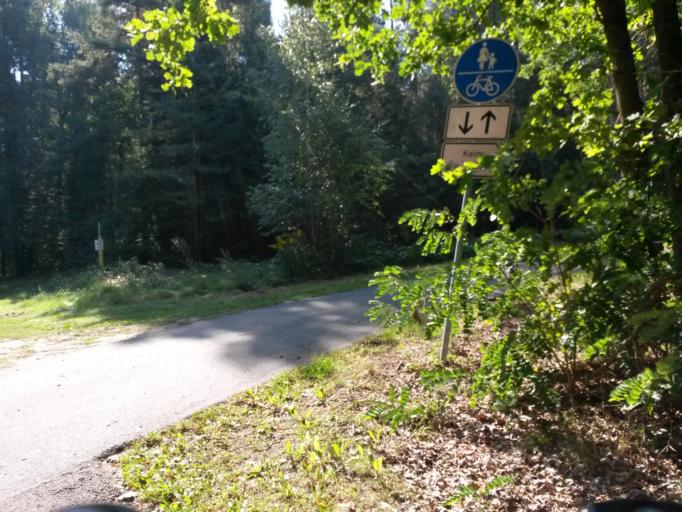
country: DE
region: Brandenburg
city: Templin
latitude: 53.0574
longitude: 13.4105
